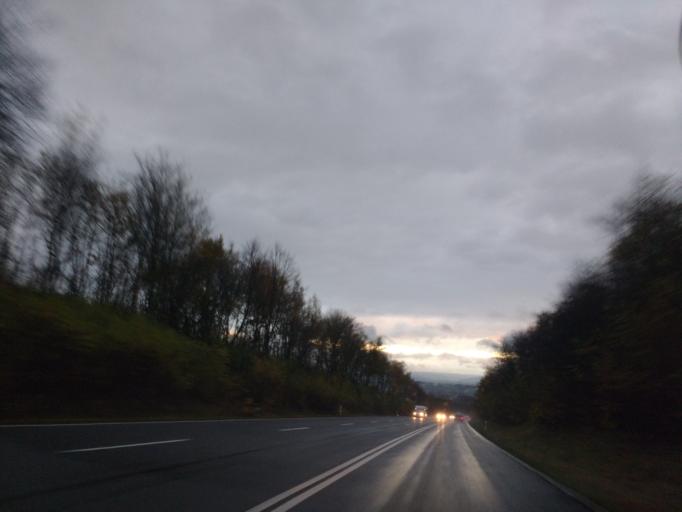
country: DE
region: Hesse
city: Niedenstein
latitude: 51.2769
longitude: 9.3429
